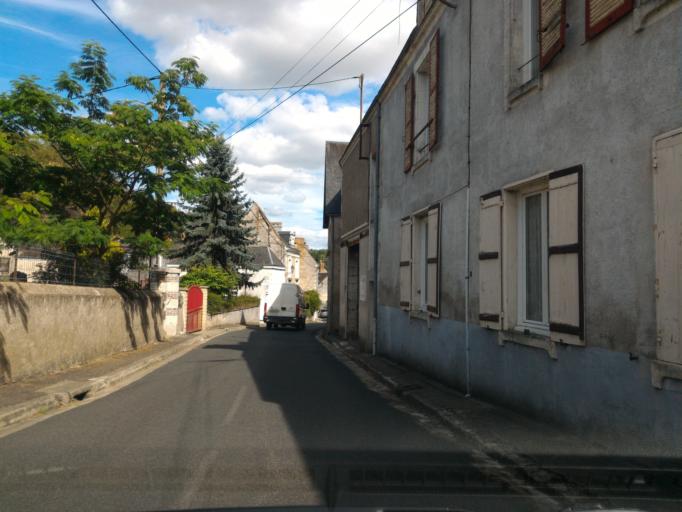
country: FR
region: Centre
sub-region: Departement d'Indre-et-Loire
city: Cangey
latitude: 47.4597
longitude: 1.0388
